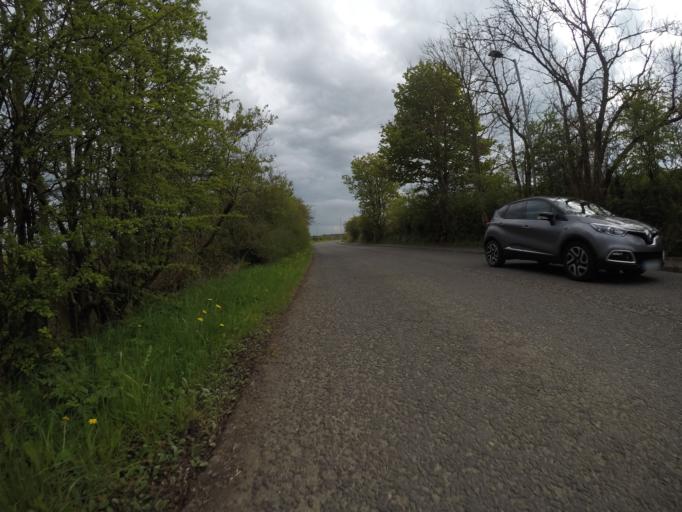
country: GB
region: Scotland
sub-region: East Ayrshire
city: Kilmarnock
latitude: 55.6518
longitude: -4.4488
